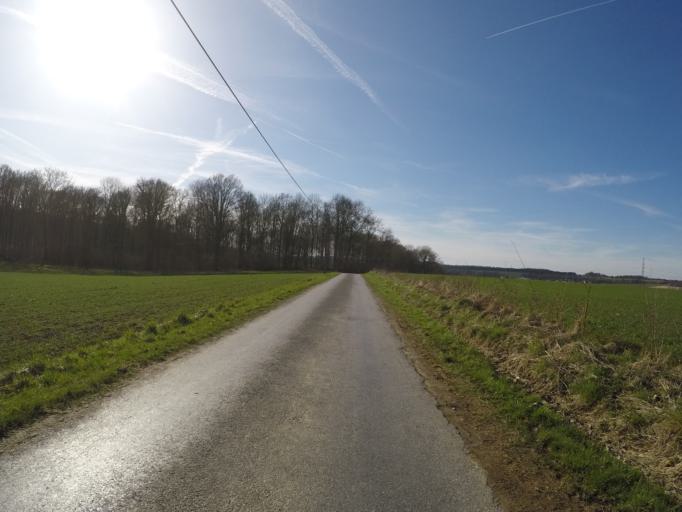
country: BE
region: Wallonia
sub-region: Province de Namur
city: Hamois
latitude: 50.3439
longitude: 5.1320
